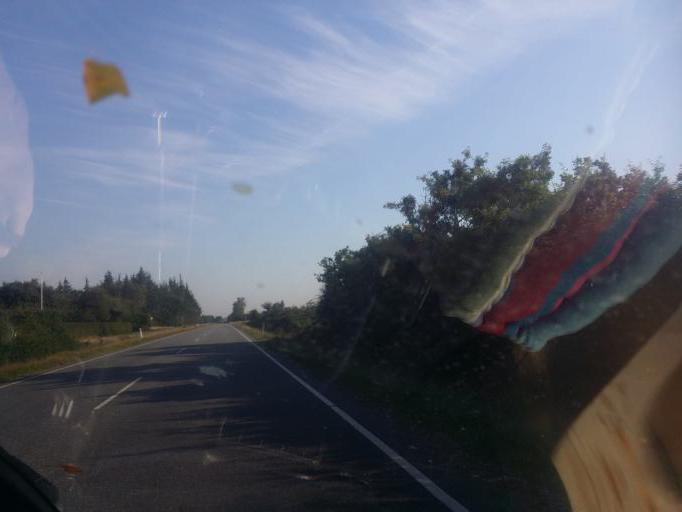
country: DK
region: South Denmark
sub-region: Esbjerg Kommune
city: Ribe
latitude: 55.2961
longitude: 8.7404
